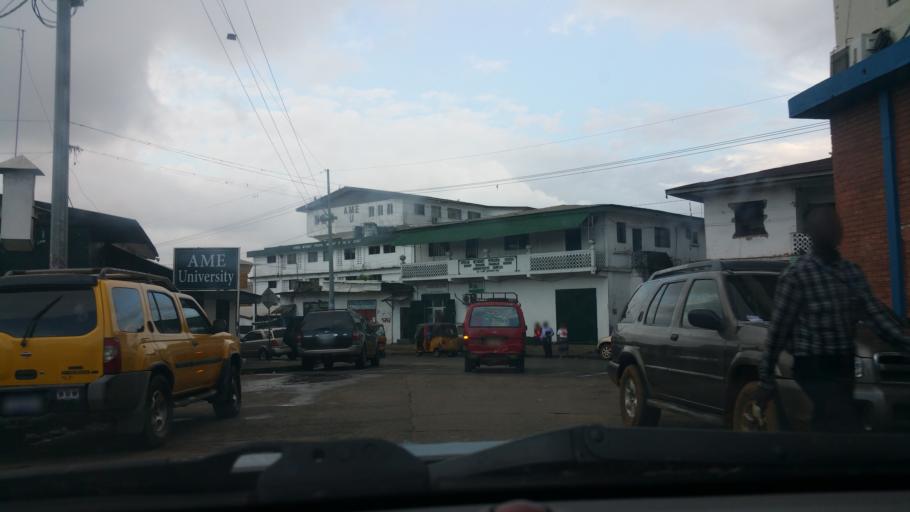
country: LR
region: Montserrado
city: Monrovia
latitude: 6.3115
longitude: -10.8009
